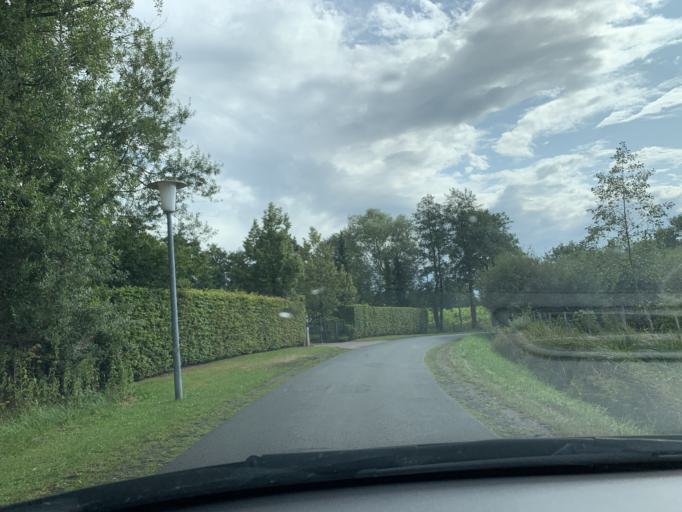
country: DE
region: Lower Saxony
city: Westerstede
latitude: 53.2655
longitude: 7.9003
